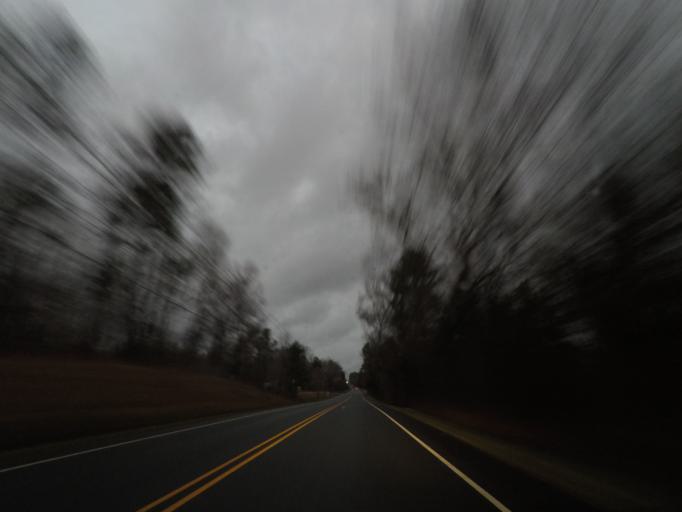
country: US
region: North Carolina
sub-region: Orange County
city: Hillsborough
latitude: 36.1189
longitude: -79.1141
